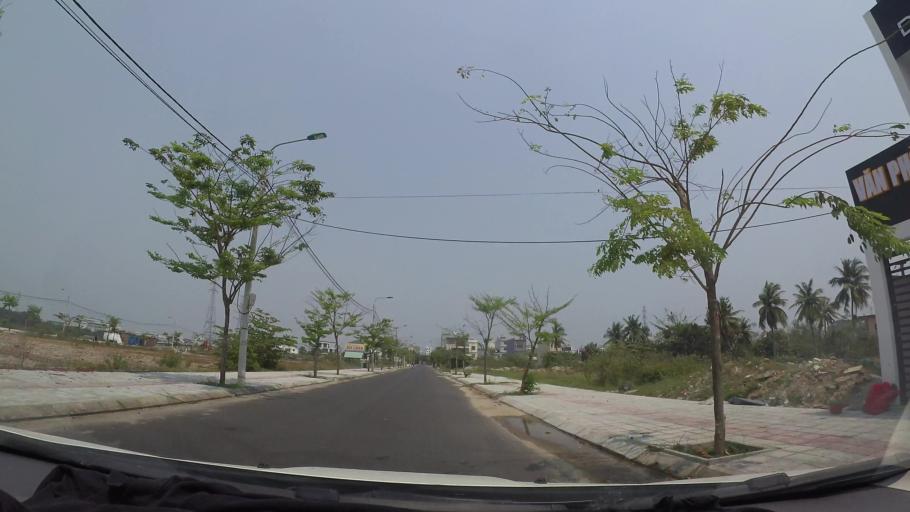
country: VN
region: Da Nang
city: Cam Le
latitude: 16.0198
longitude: 108.2225
